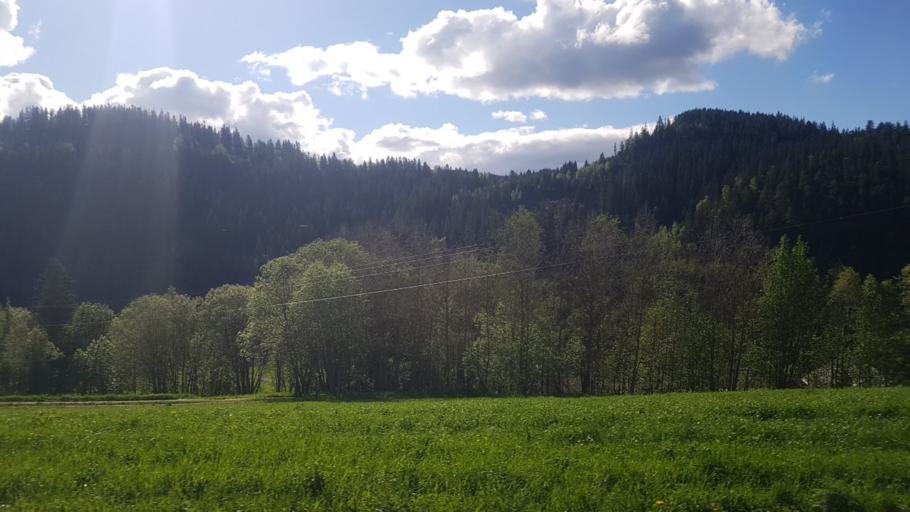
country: NO
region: Sor-Trondelag
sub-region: Midtre Gauldal
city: Storen
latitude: 62.9784
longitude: 10.2220
